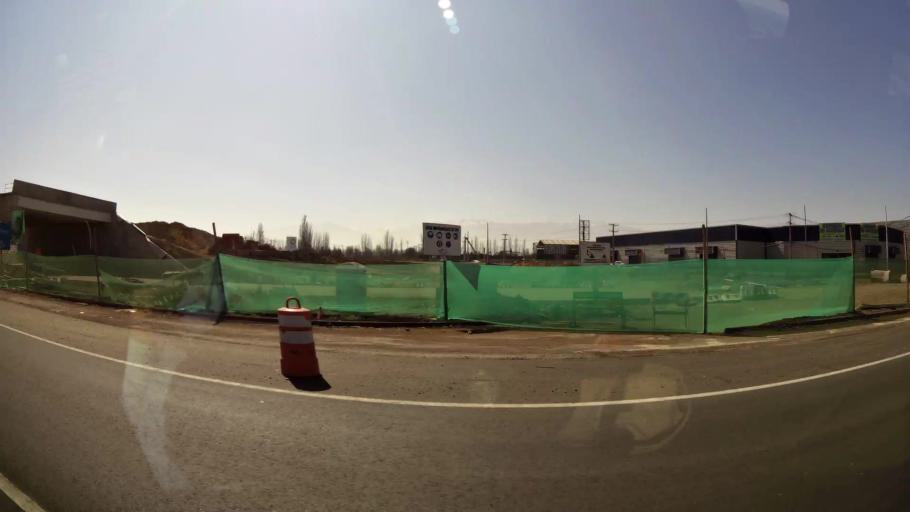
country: CL
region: Santiago Metropolitan
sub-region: Provincia de Chacabuco
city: Chicureo Abajo
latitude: -33.2738
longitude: -70.7416
